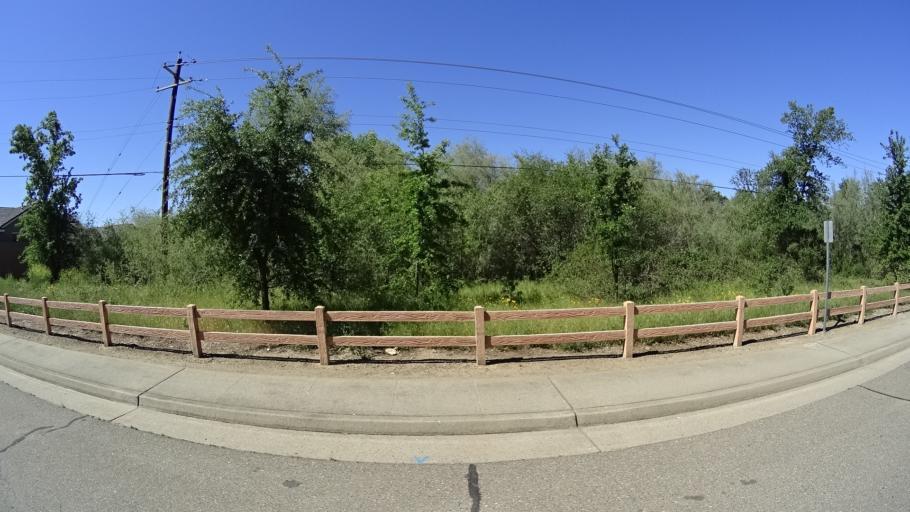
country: US
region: California
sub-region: Placer County
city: Rocklin
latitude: 38.8013
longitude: -121.2149
